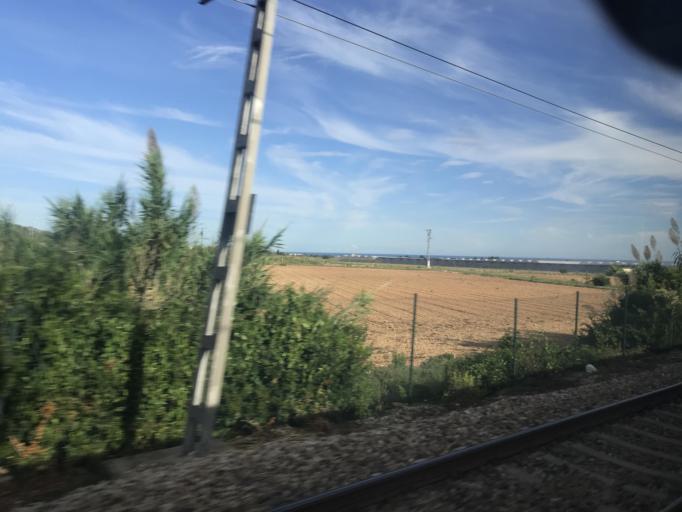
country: ES
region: Catalonia
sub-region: Provincia de Tarragona
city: Alcanar
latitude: 40.5461
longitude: 0.4309
